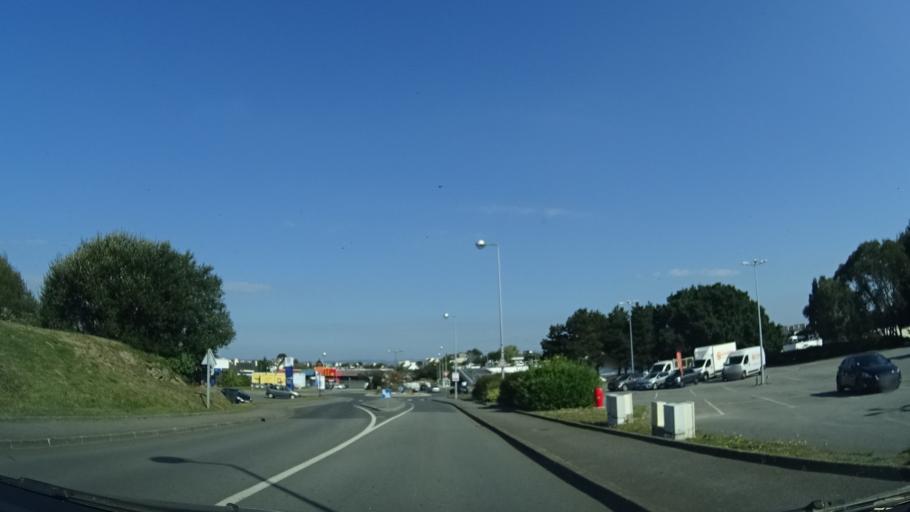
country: FR
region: Brittany
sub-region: Departement du Finistere
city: Douarnenez
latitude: 48.0901
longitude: -4.3467
